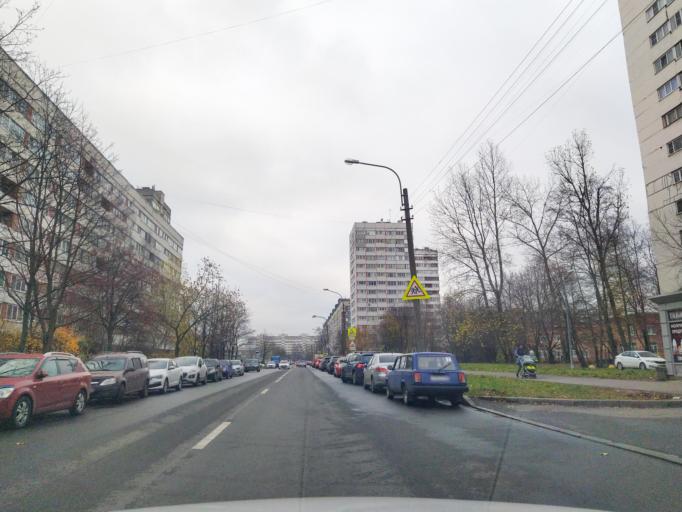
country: RU
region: St.-Petersburg
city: Sosnovka
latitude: 60.0426
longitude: 30.3536
